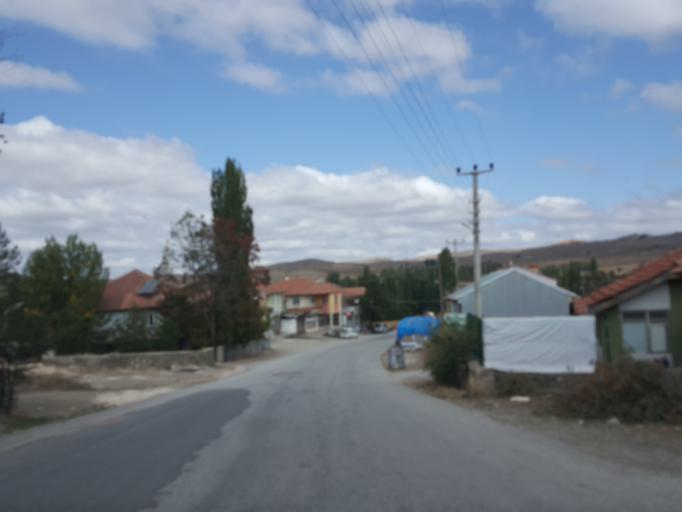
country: TR
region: Sivas
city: Yavu
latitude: 39.7928
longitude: 36.2046
